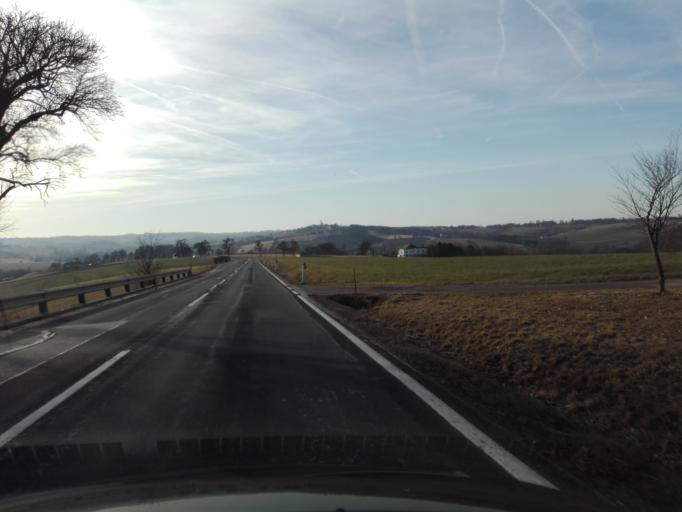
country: AT
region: Lower Austria
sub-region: Politischer Bezirk Amstetten
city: Strengberg
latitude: 48.1400
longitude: 14.6890
